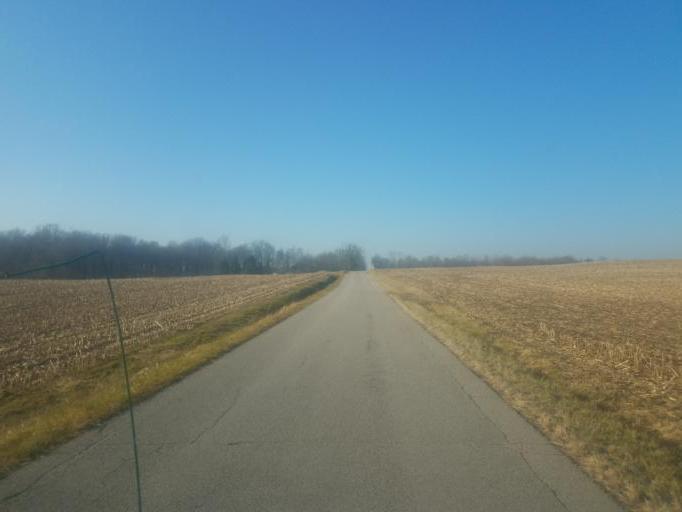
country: US
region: Ohio
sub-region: Crawford County
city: Bucyrus
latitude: 40.8294
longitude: -82.9232
